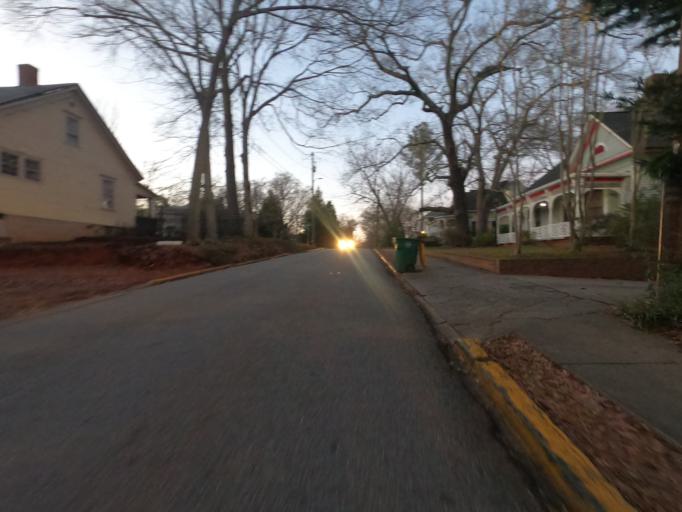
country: US
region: Georgia
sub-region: Clarke County
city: Athens
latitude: 33.9507
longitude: -83.3840
